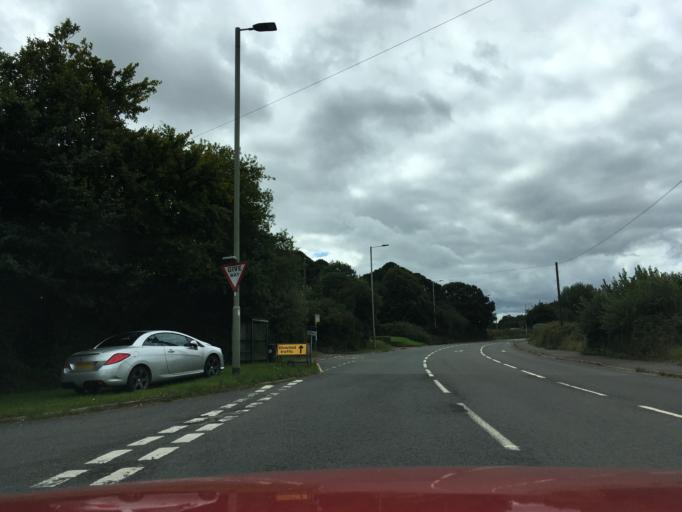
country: GB
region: England
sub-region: Devon
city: Heavitree
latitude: 50.7577
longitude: -3.4424
